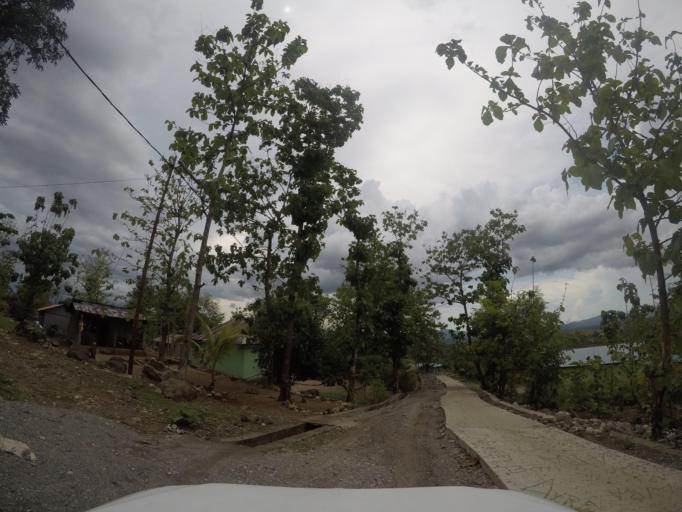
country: TL
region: Bobonaro
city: Maliana
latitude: -8.9966
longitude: 125.2125
